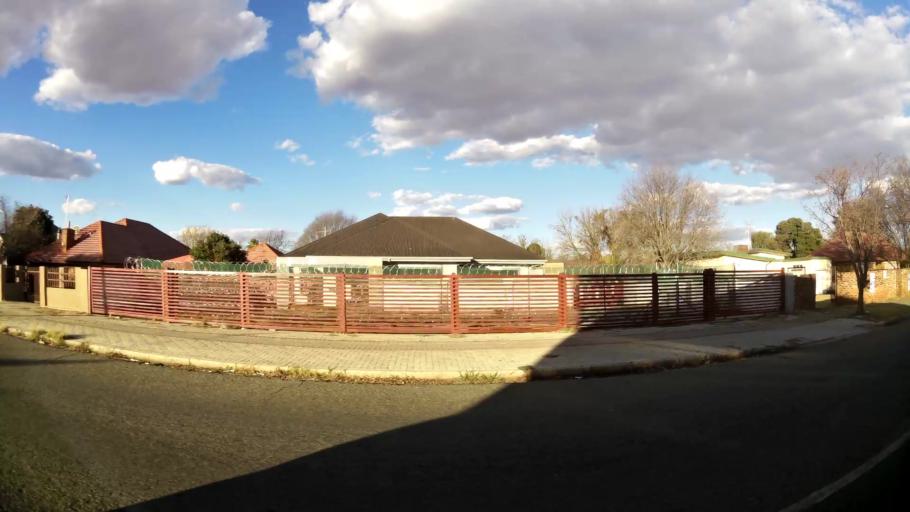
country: ZA
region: North-West
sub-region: Dr Kenneth Kaunda District Municipality
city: Potchefstroom
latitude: -26.7221
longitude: 27.0964
